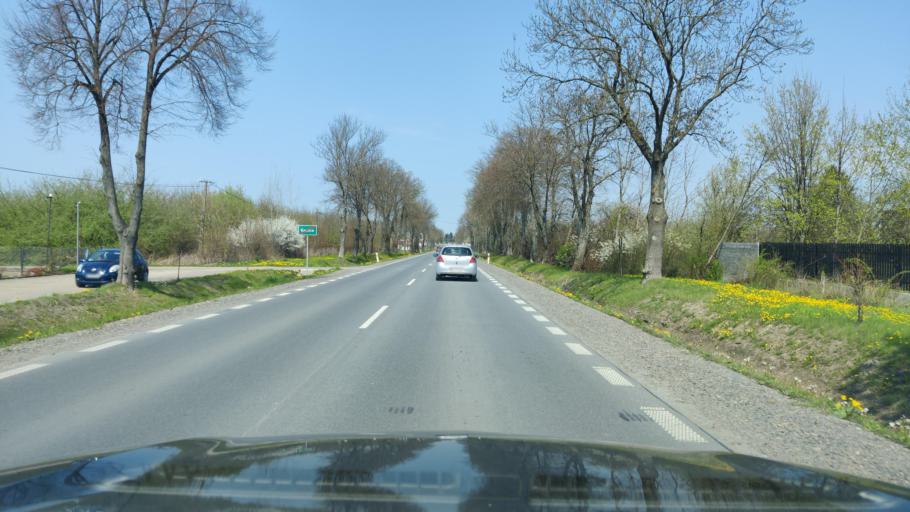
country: PL
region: Masovian Voivodeship
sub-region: Powiat pultuski
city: Pultusk
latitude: 52.6827
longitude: 21.0809
